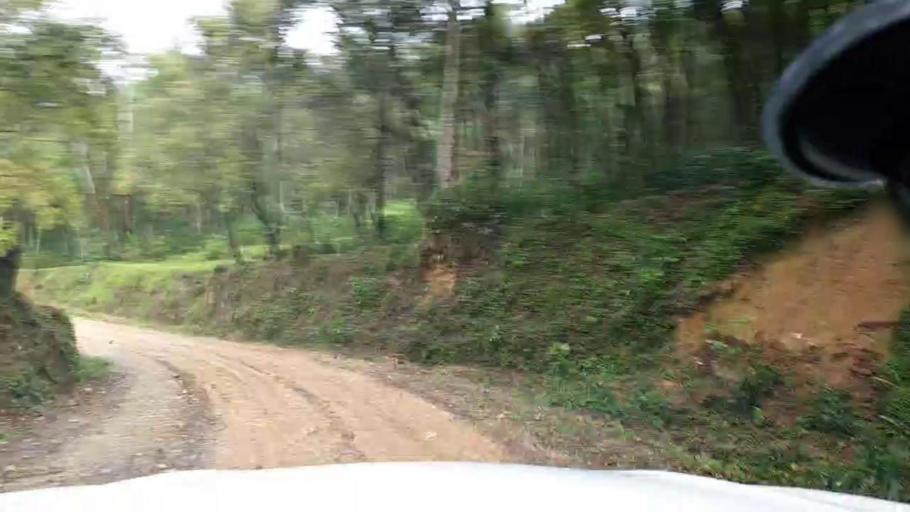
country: RW
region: Western Province
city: Kibuye
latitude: -2.1175
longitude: 29.4928
